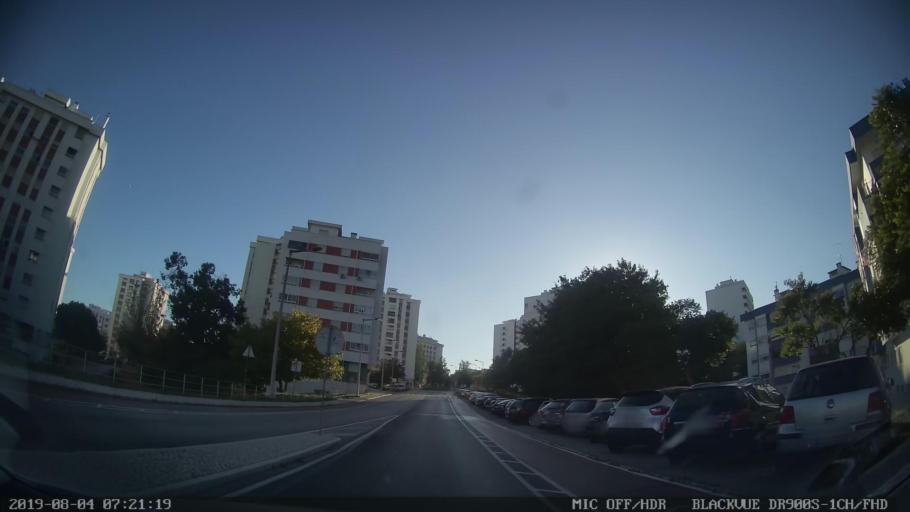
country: PT
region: Lisbon
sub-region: Vila Franca de Xira
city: Povoa de Santa Iria
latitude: 38.8601
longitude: -9.0696
